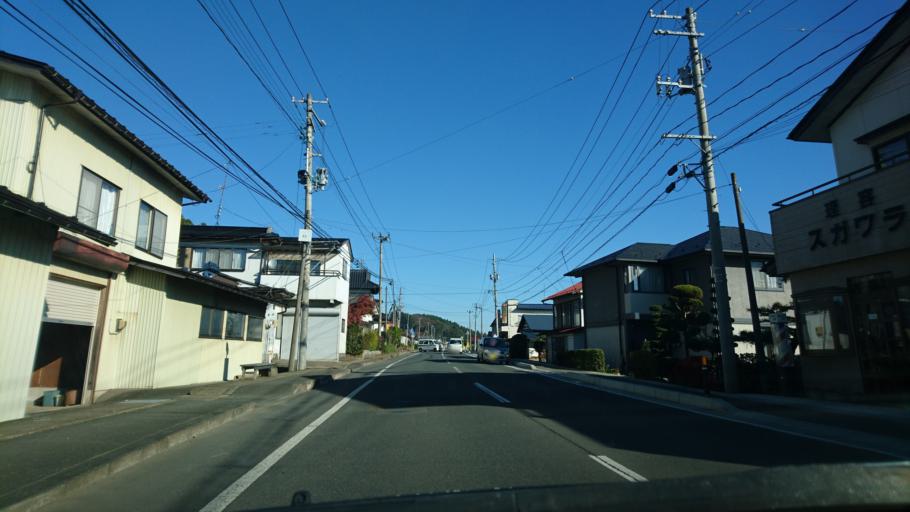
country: JP
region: Iwate
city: Mizusawa
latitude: 39.0680
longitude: 141.1280
